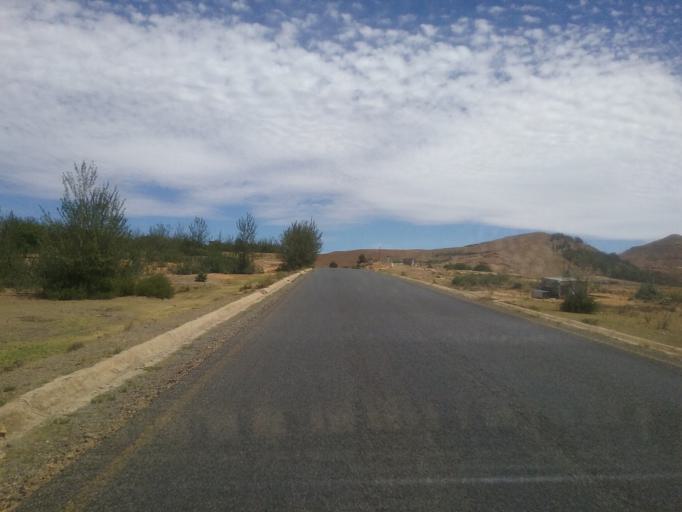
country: LS
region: Mafeteng
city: Mafeteng
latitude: -29.9208
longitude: 27.2518
